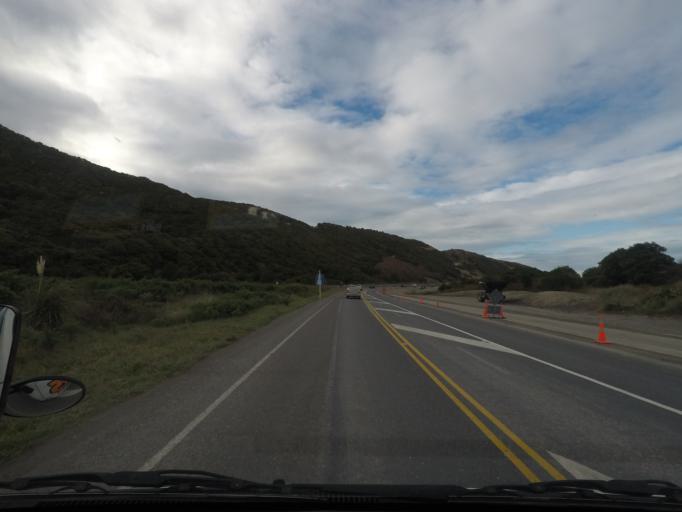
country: NZ
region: Canterbury
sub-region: Kaikoura District
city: Kaikoura
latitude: -42.2170
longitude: 173.8603
